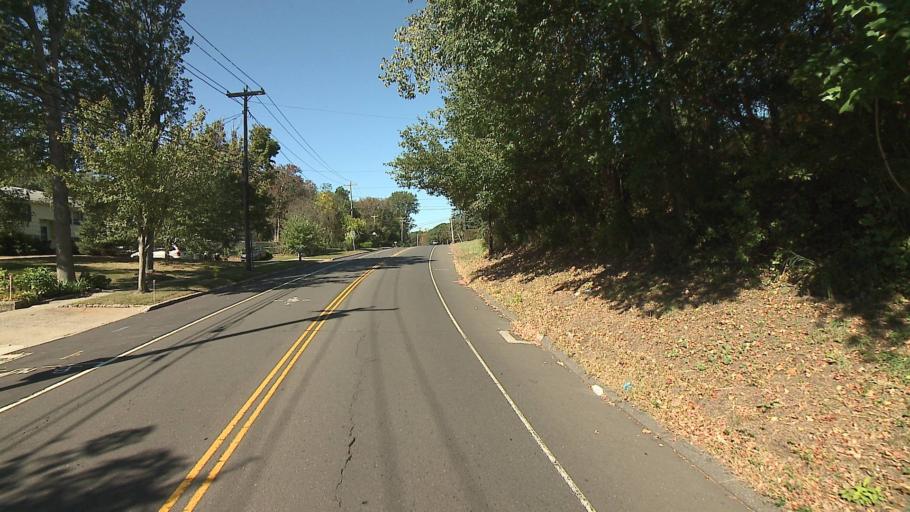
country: US
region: Connecticut
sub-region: New Haven County
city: Woodmont
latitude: 41.2259
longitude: -73.0169
